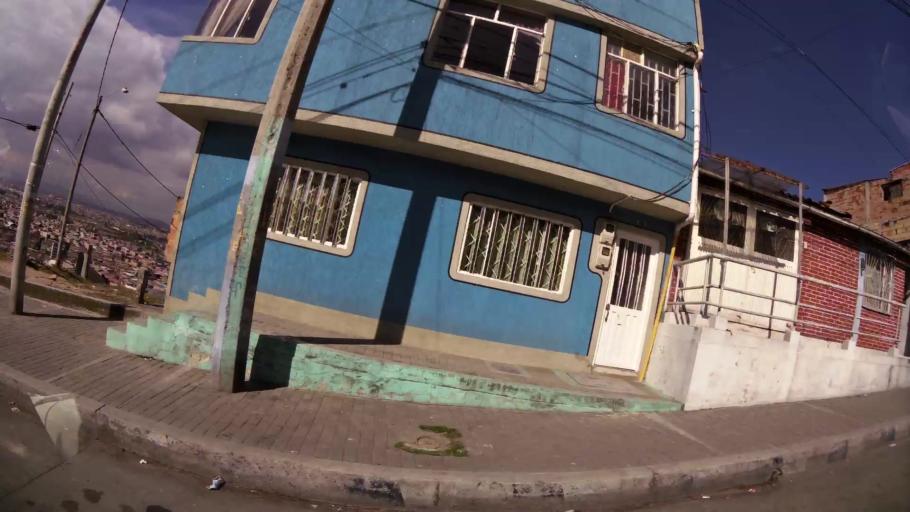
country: CO
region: Cundinamarca
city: Soacha
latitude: 4.5557
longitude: -74.1449
